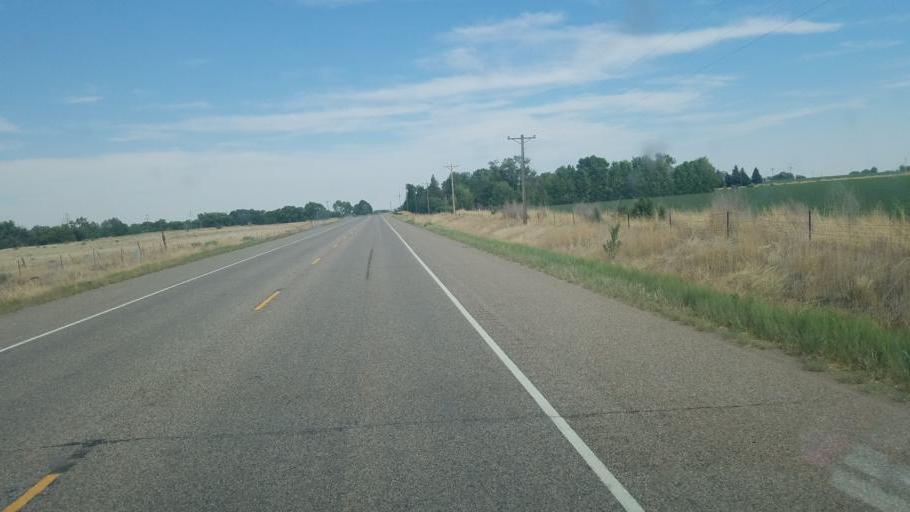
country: US
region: Colorado
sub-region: Otero County
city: Fowler
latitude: 38.2301
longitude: -104.2985
